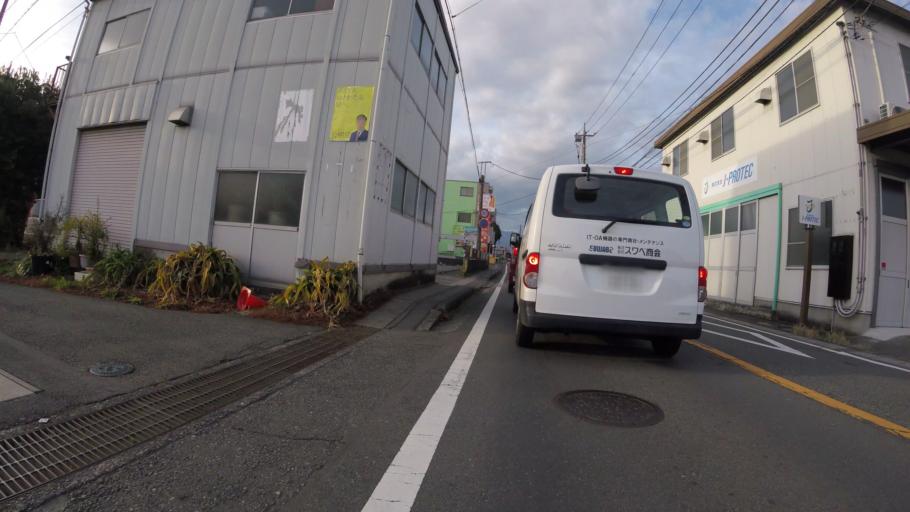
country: JP
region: Shizuoka
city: Mishima
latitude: 35.1093
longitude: 138.9280
